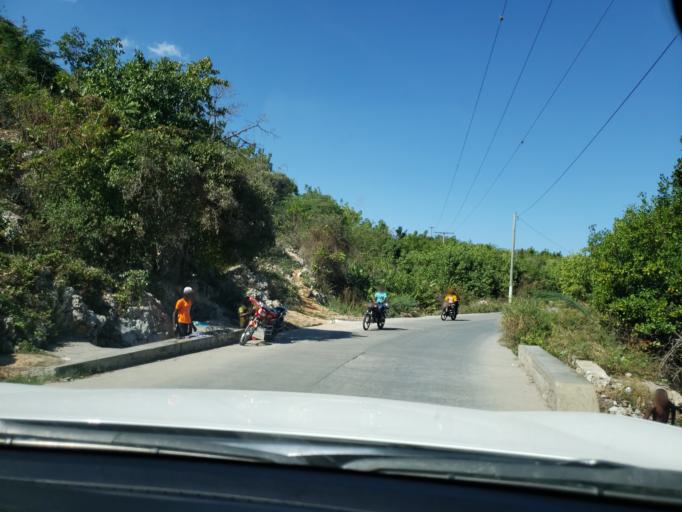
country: HT
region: Nippes
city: Miragoane
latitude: 18.4442
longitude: -73.1015
